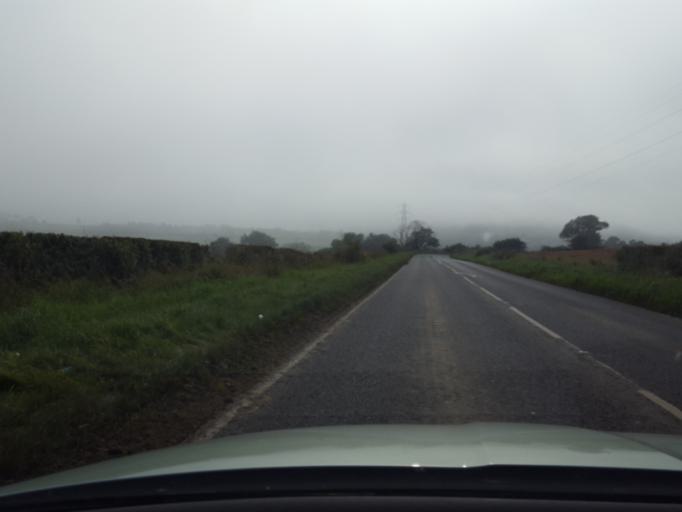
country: GB
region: Scotland
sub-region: Fife
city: Crossgates
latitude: 56.0488
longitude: -3.3848
